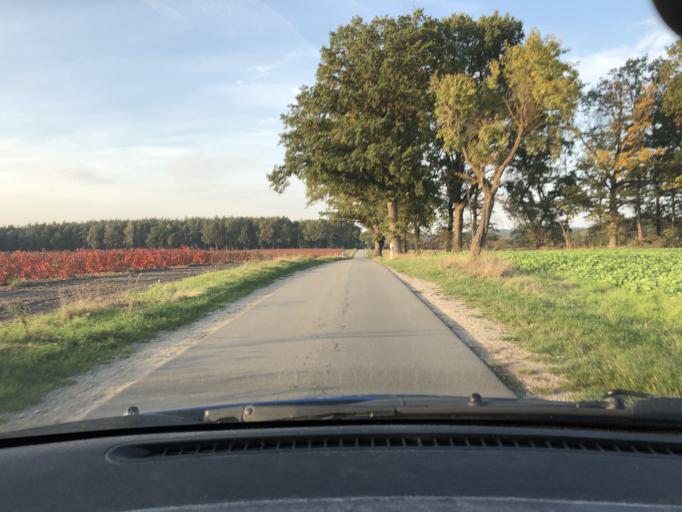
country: DE
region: Lower Saxony
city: Hitzacker
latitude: 53.1375
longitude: 11.0076
